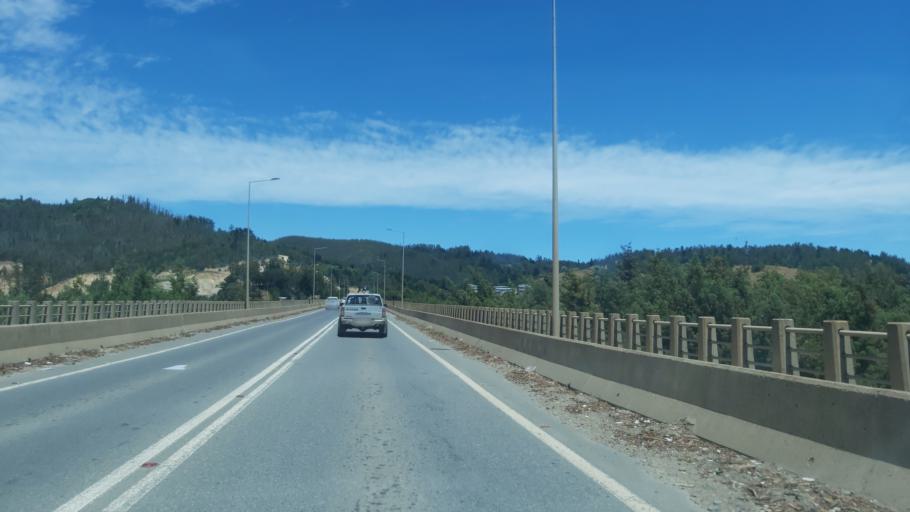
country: CL
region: Maule
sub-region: Provincia de Talca
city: Constitucion
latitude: -35.3389
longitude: -72.3911
